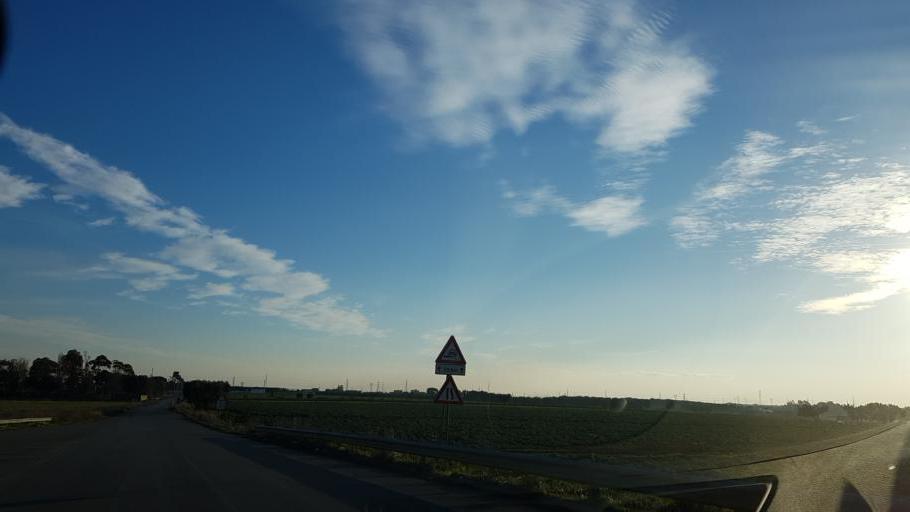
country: IT
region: Apulia
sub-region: Provincia di Brindisi
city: La Rosa
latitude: 40.6170
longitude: 17.9450
